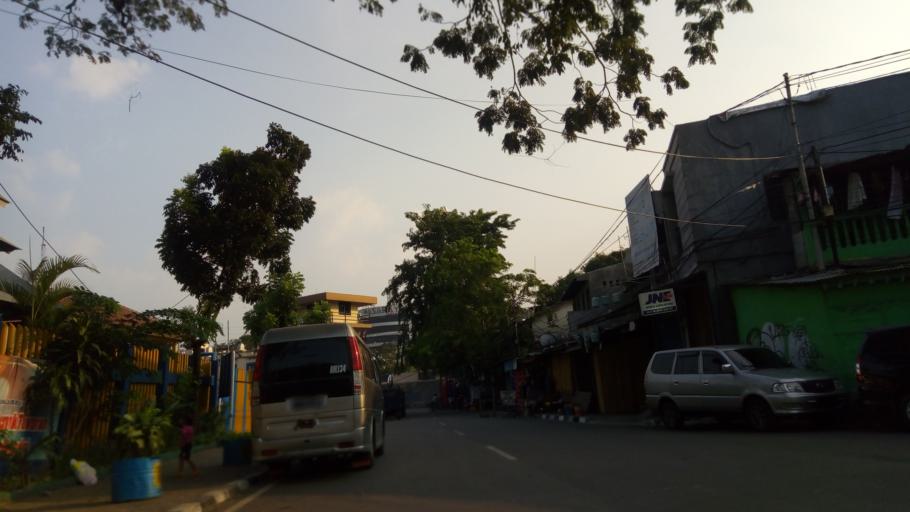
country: ID
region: Jakarta Raya
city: Jakarta
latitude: -6.2071
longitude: 106.8487
